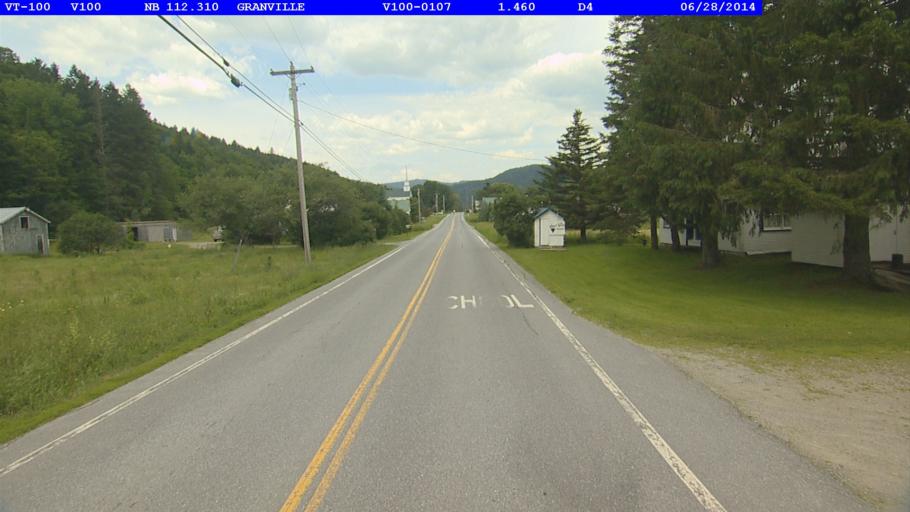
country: US
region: Vermont
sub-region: Orange County
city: Randolph
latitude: 43.9654
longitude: -72.8423
